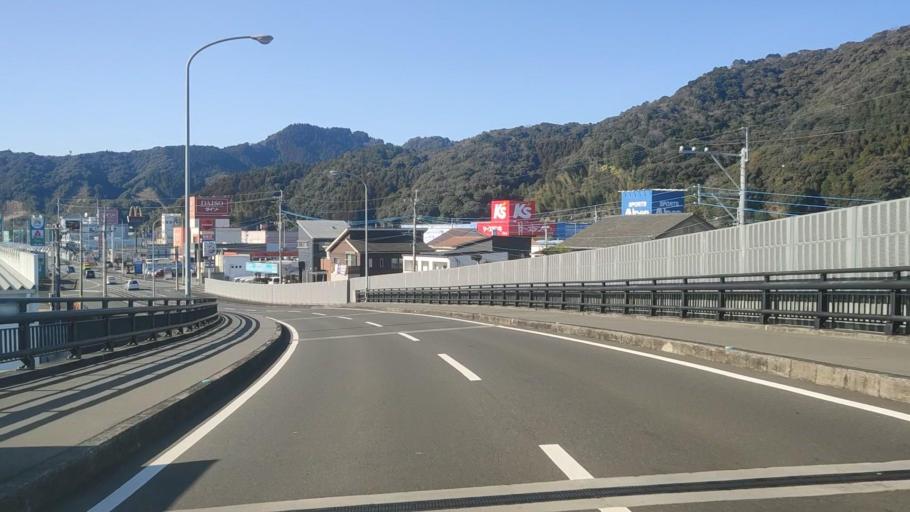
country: JP
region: Oita
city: Saiki
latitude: 32.9608
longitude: 131.8702
